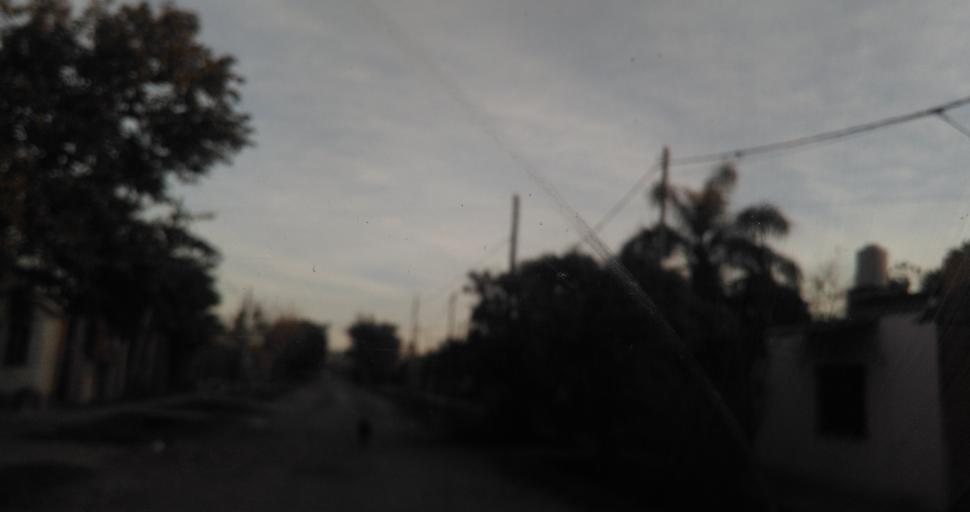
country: AR
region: Chaco
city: Resistencia
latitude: -27.4671
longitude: -59.0081
